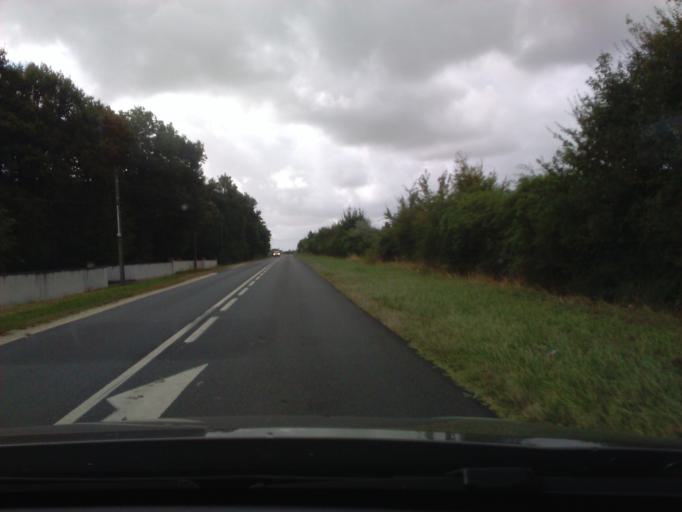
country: FR
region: Centre
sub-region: Departement du Loir-et-Cher
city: Cormeray
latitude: 47.4997
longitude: 1.4055
